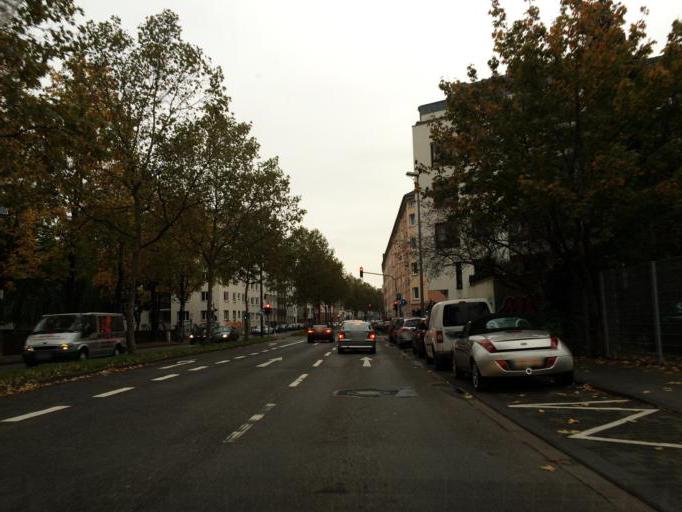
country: DE
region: North Rhine-Westphalia
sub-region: Regierungsbezirk Koln
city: Neustadt/Nord
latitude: 50.9452
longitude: 6.9494
